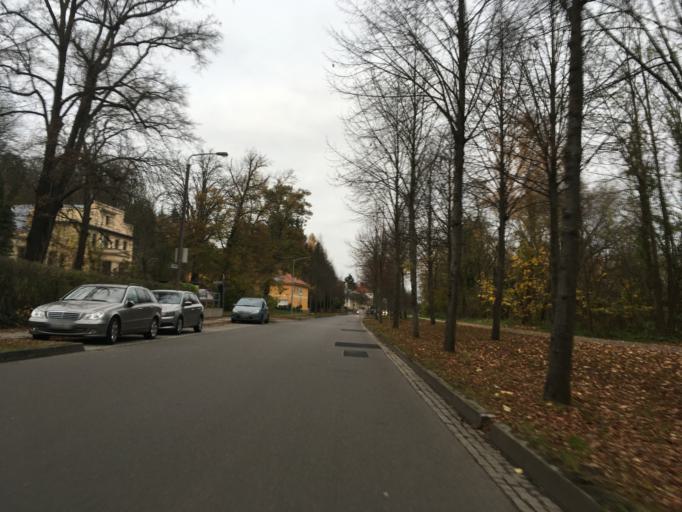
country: DE
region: Brandenburg
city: Frankfurt (Oder)
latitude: 52.3219
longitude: 14.5537
